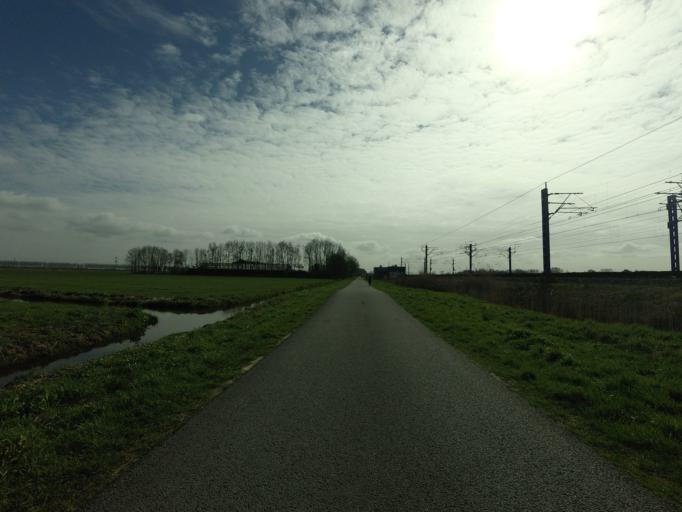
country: NL
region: North Holland
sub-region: Gemeente Amsterdam
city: Amsterdam-Zuidoost
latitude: 52.2625
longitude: 4.9918
